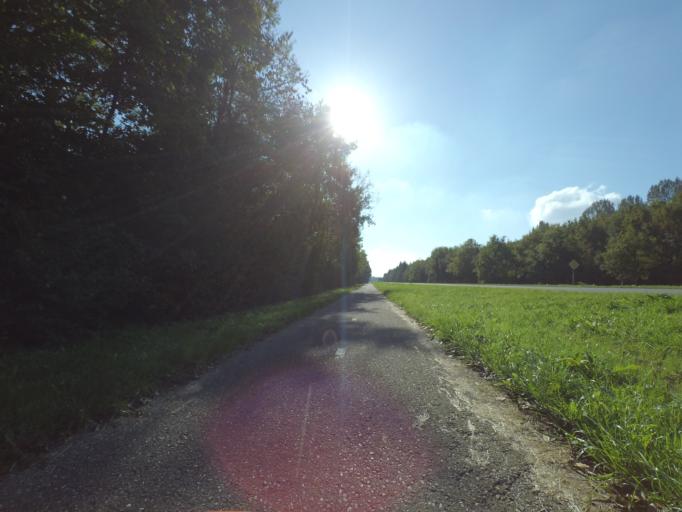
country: NL
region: Flevoland
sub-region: Gemeente Zeewolde
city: Zeewolde
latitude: 52.3030
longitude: 5.5140
